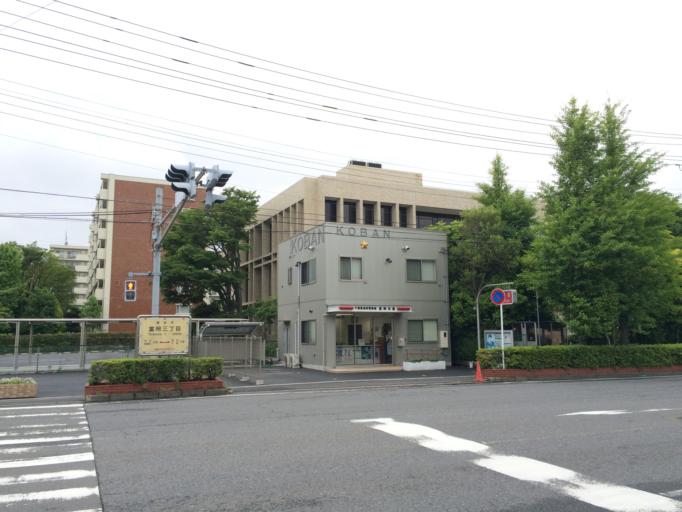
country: JP
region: Tokyo
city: Urayasu
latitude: 35.6410
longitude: 139.9019
